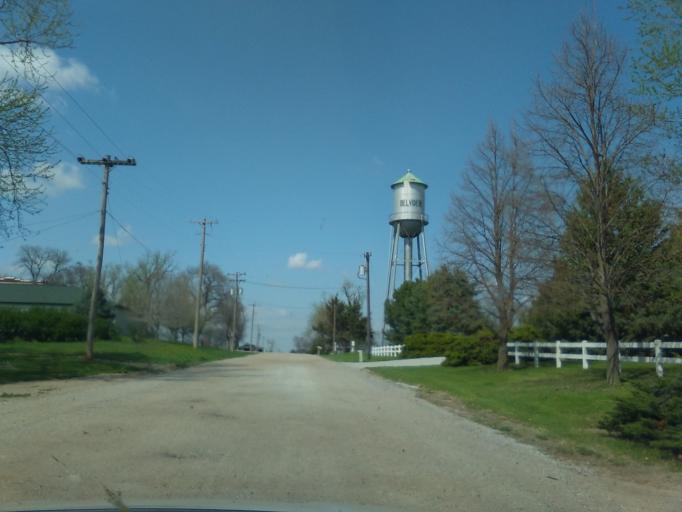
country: US
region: Nebraska
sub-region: Thayer County
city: Hebron
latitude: 40.2540
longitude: -97.5579
